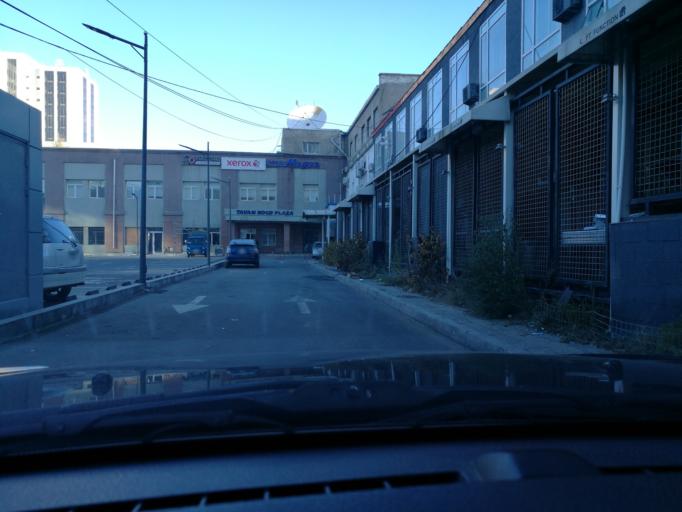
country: MN
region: Ulaanbaatar
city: Ulaanbaatar
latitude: 47.9206
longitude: 106.9203
